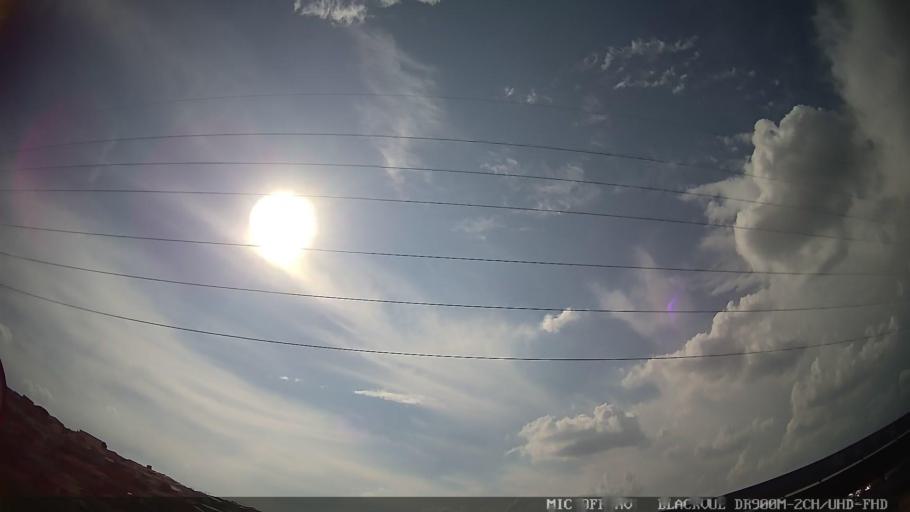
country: BR
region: Sao Paulo
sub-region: Braganca Paulista
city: Braganca Paulista
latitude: -22.9457
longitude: -46.5566
